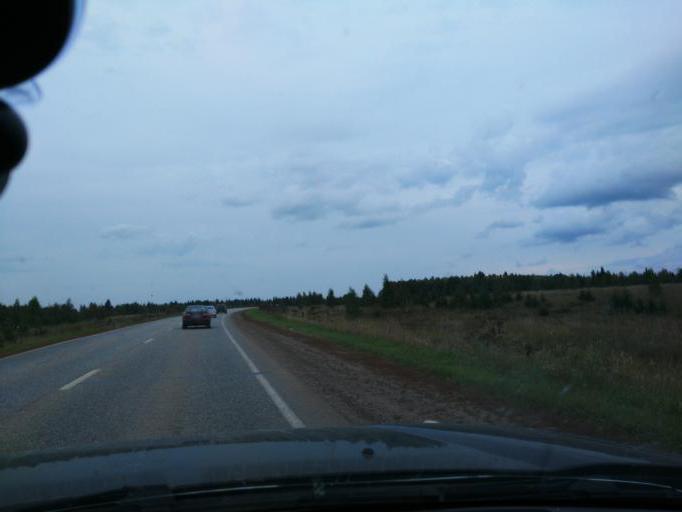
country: RU
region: Perm
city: Chernushka
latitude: 56.5245
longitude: 56.0224
